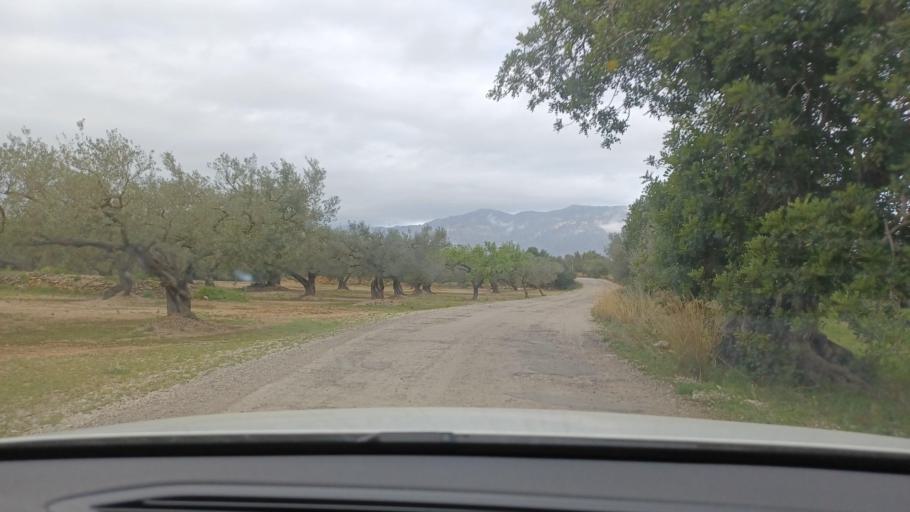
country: ES
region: Catalonia
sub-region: Provincia de Tarragona
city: Tortosa
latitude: 40.7916
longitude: 0.4739
